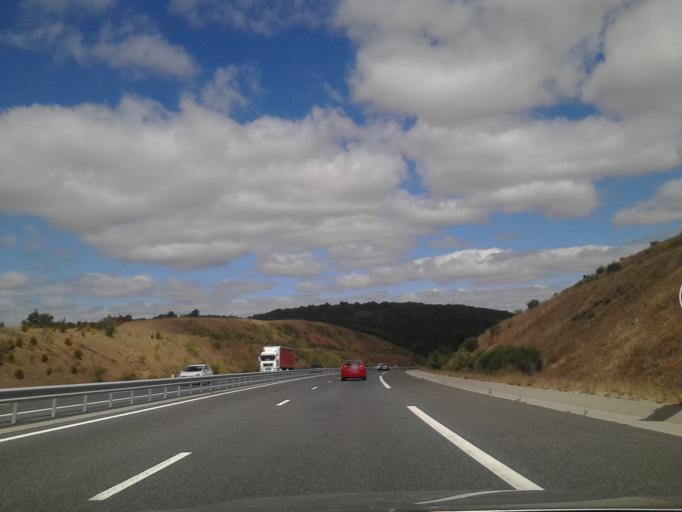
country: FR
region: Midi-Pyrenees
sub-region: Departement de l'Aveyron
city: Creissels
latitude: 44.0596
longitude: 3.0305
